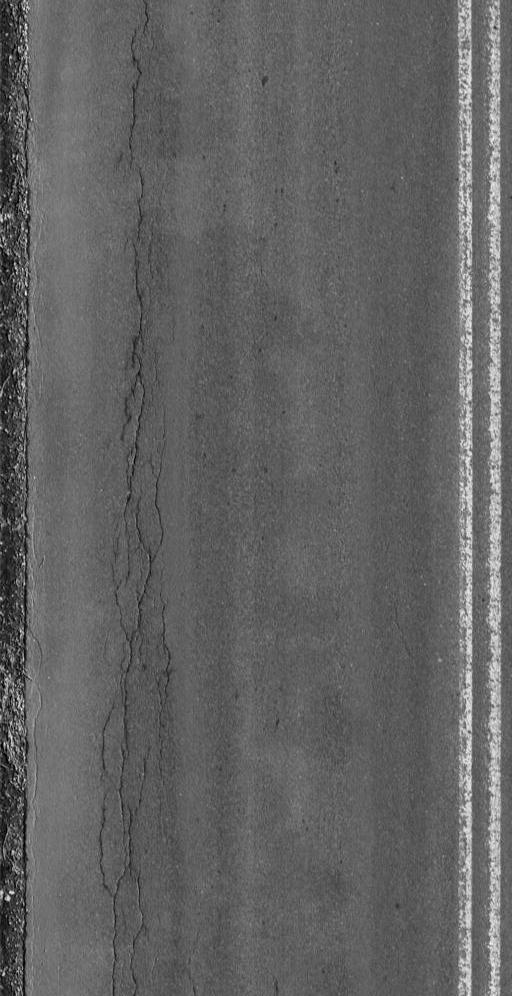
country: US
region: Vermont
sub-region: Windham County
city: Bellows Falls
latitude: 43.1188
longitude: -72.4649
